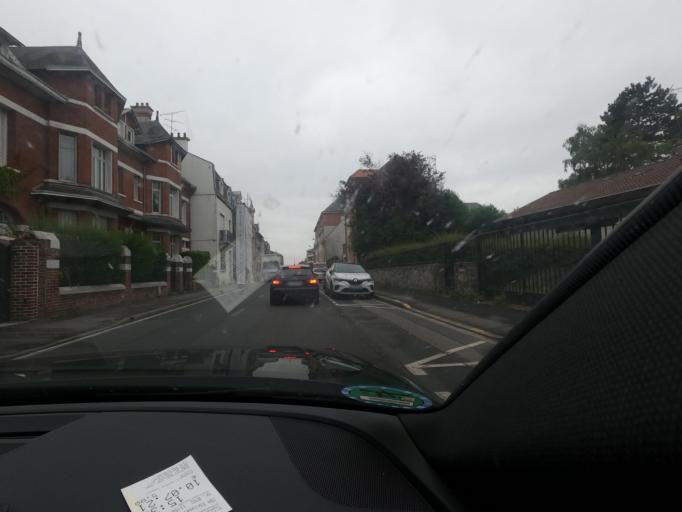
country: FR
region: Picardie
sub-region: Departement de la Somme
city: Amiens
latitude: 49.8799
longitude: 2.3049
